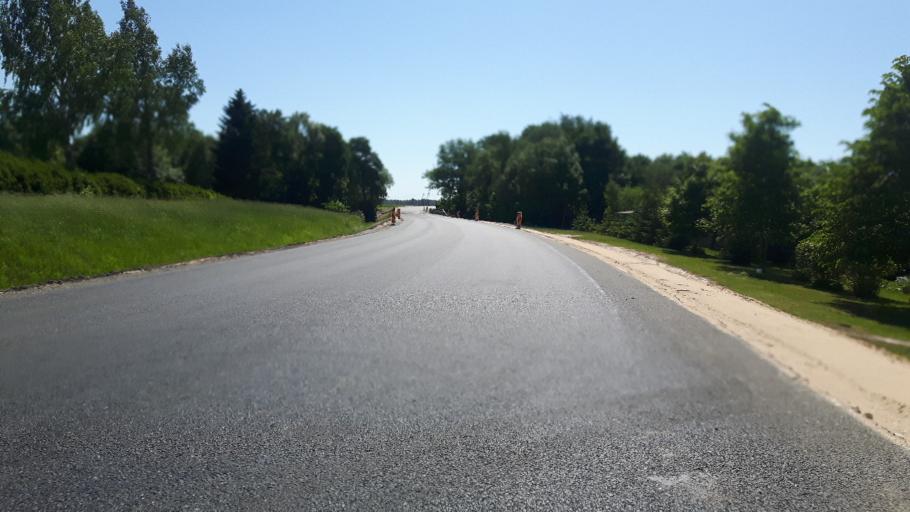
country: EE
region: Paernumaa
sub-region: Sindi linn
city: Sindi
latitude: 58.4219
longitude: 24.7152
